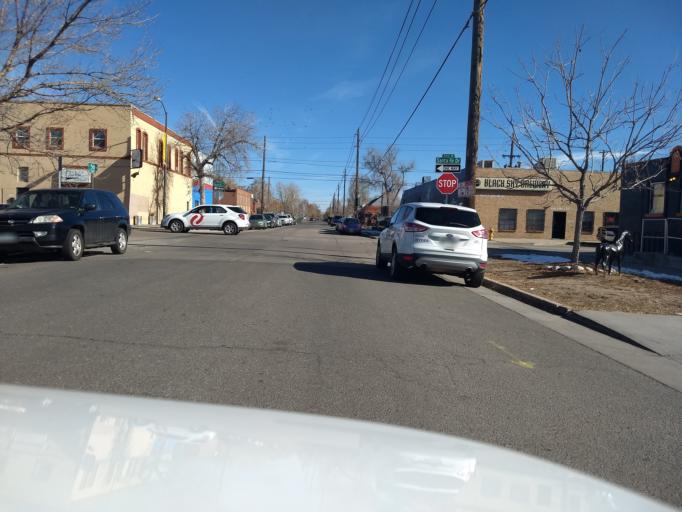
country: US
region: Colorado
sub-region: Denver County
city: Denver
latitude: 39.7241
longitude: -104.9989
